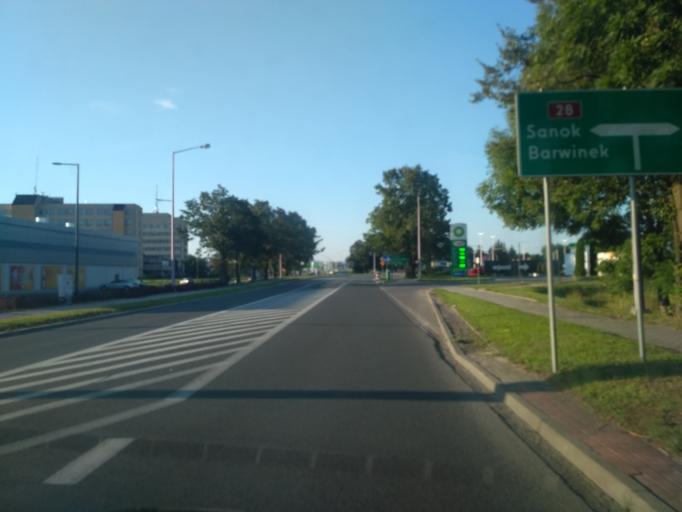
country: PL
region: Subcarpathian Voivodeship
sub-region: Krosno
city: Krosno
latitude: 49.6810
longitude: 21.7725
